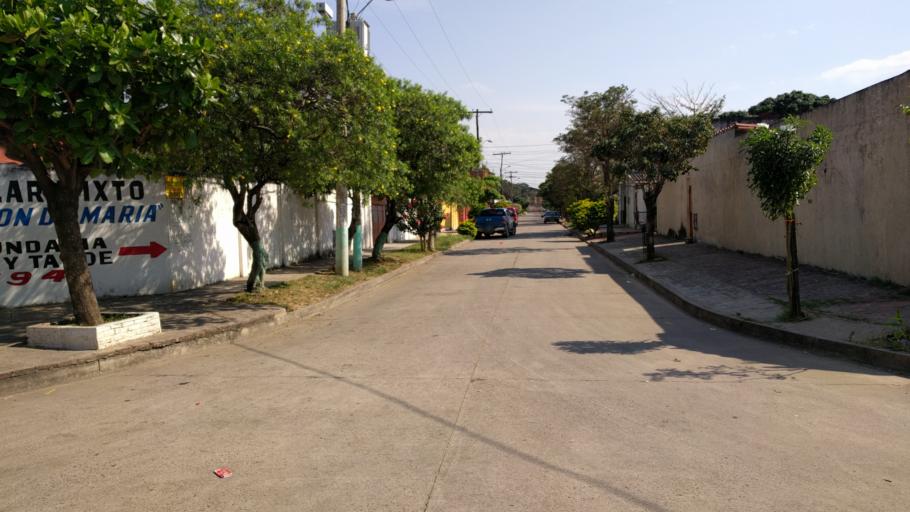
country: BO
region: Santa Cruz
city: Santa Cruz de la Sierra
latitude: -17.8151
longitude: -63.1711
